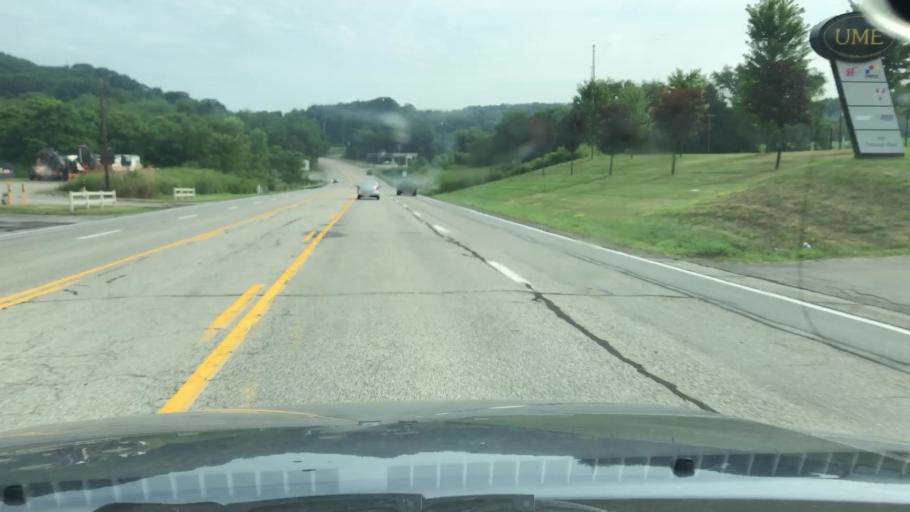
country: US
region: Pennsylvania
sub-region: Butler County
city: Nixon
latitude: 40.7312
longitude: -79.9249
